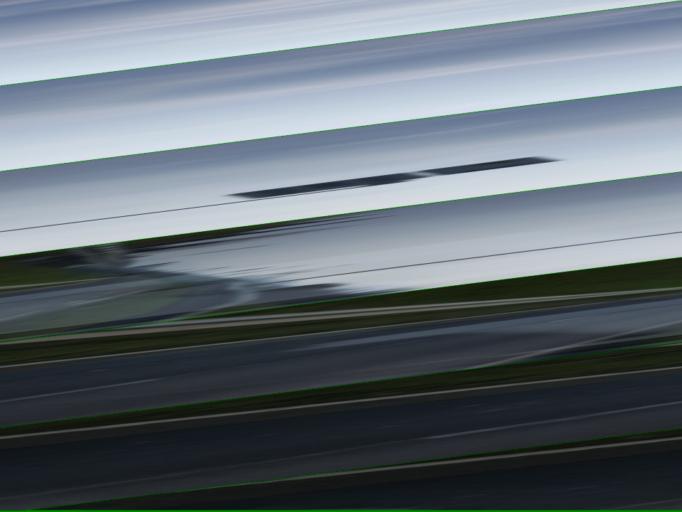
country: FR
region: Ile-de-France
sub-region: Departement des Yvelines
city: Houdan
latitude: 48.7727
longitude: 1.5551
